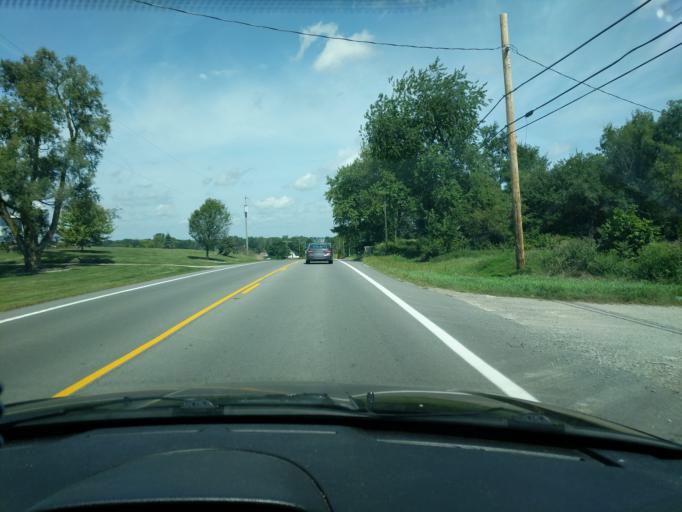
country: US
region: Ohio
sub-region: Logan County
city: Bellefontaine
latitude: 40.3102
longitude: -83.7599
